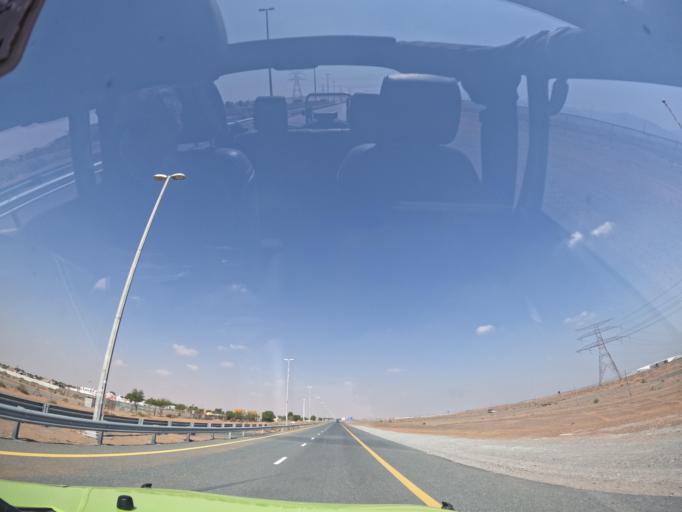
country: AE
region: Ash Shariqah
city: Adh Dhayd
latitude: 24.8067
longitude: 55.7981
